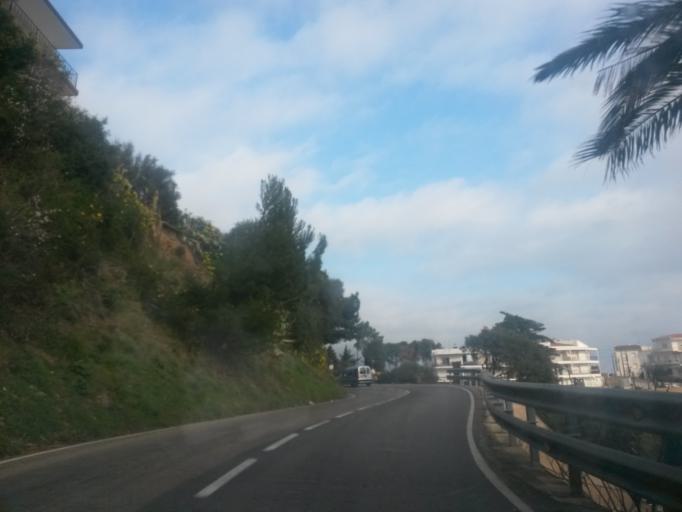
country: ES
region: Catalonia
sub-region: Provincia de Girona
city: Llanca
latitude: 42.3605
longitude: 3.1619
